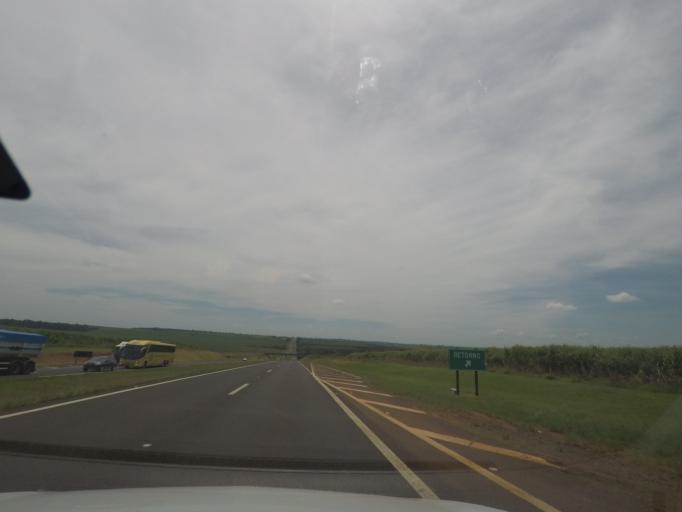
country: BR
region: Sao Paulo
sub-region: Bebedouro
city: Bebedouro
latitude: -21.0429
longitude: -48.4167
